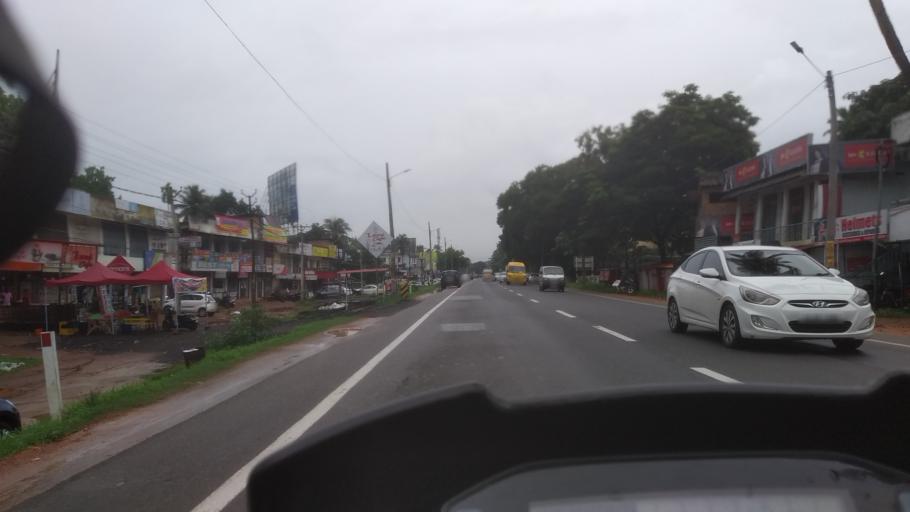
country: IN
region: Kerala
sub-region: Alappuzha
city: Kayankulam
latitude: 9.1774
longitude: 76.4939
